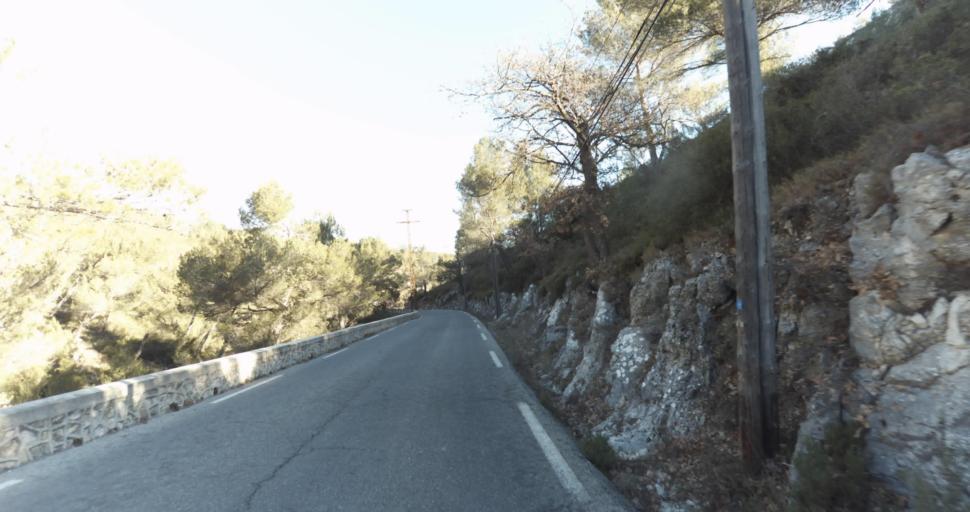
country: FR
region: Provence-Alpes-Cote d'Azur
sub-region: Departement des Bouches-du-Rhone
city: Peypin
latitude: 43.3818
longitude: 5.5681
